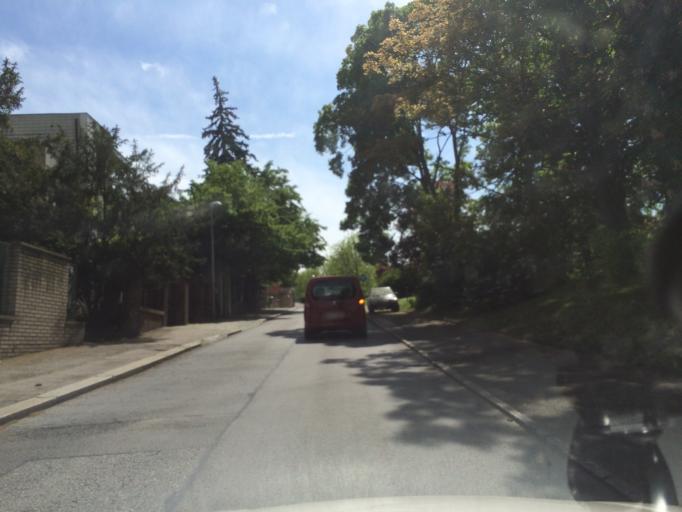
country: CZ
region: Praha
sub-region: Praha 1
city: Mala Strana
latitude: 50.0968
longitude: 14.3878
